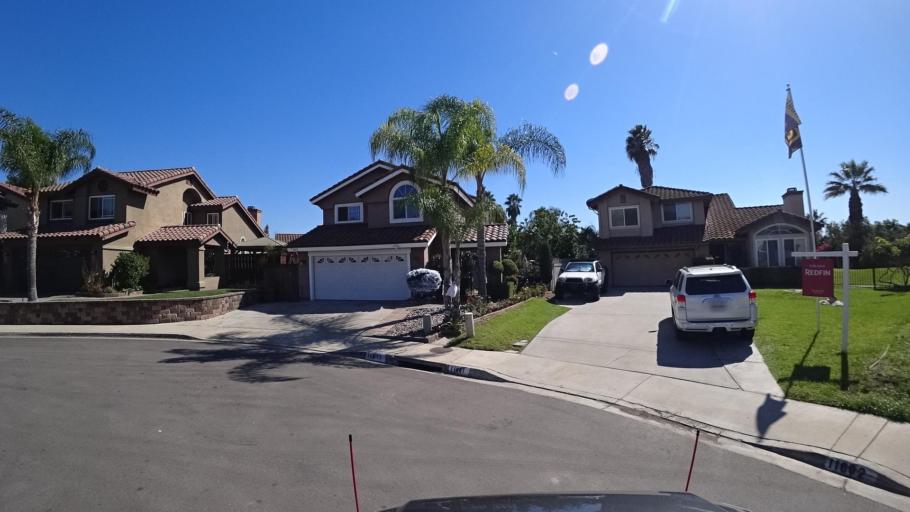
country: US
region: California
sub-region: San Diego County
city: Rancho San Diego
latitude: 32.7494
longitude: -116.9388
